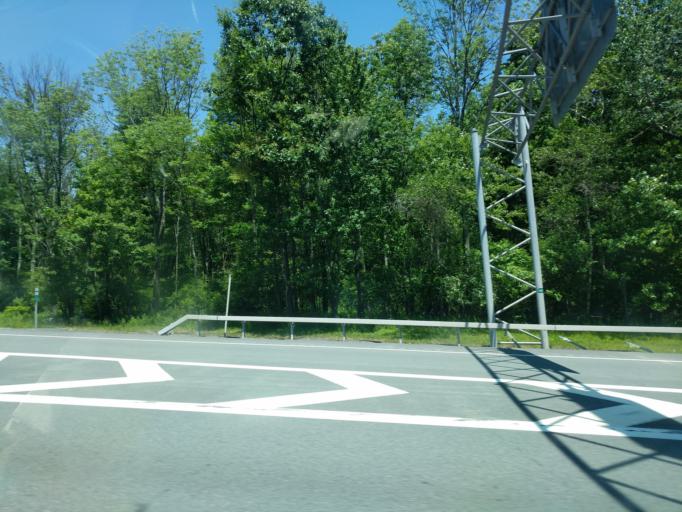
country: US
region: New York
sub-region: Sullivan County
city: Monticello
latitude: 41.6600
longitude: -74.6738
